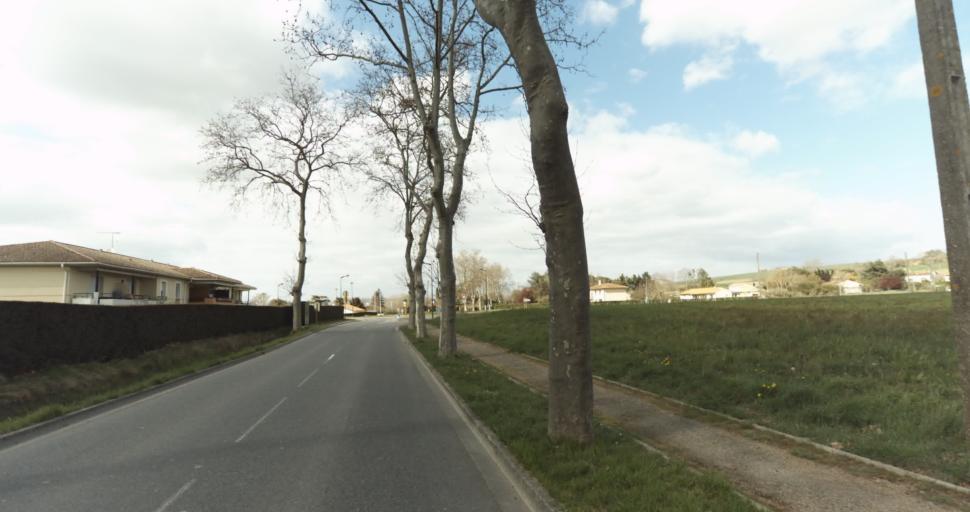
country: FR
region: Midi-Pyrenees
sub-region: Departement de la Haute-Garonne
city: Auterive
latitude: 43.3570
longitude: 1.4772
